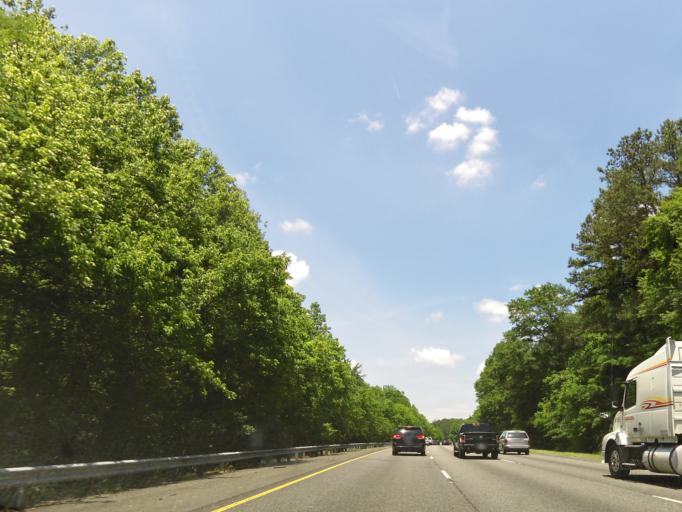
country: US
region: Georgia
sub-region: Monroe County
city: Forsyth
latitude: 33.0832
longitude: -83.9907
